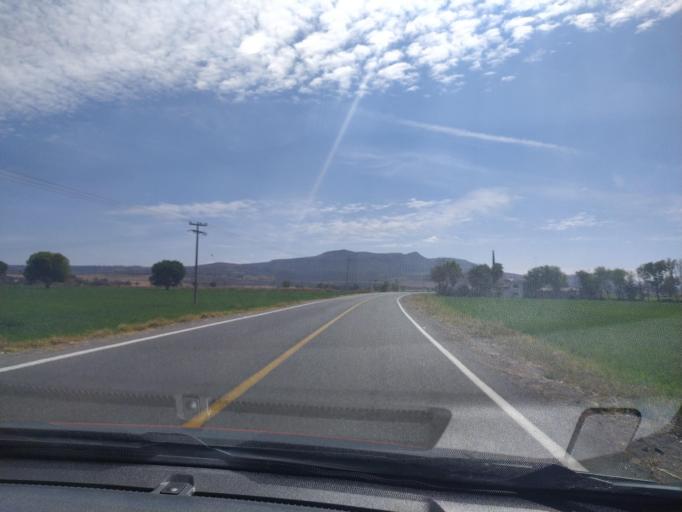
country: MX
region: Guanajuato
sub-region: San Francisco del Rincon
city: San Ignacio de Hidalgo
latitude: 20.8495
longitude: -101.8512
